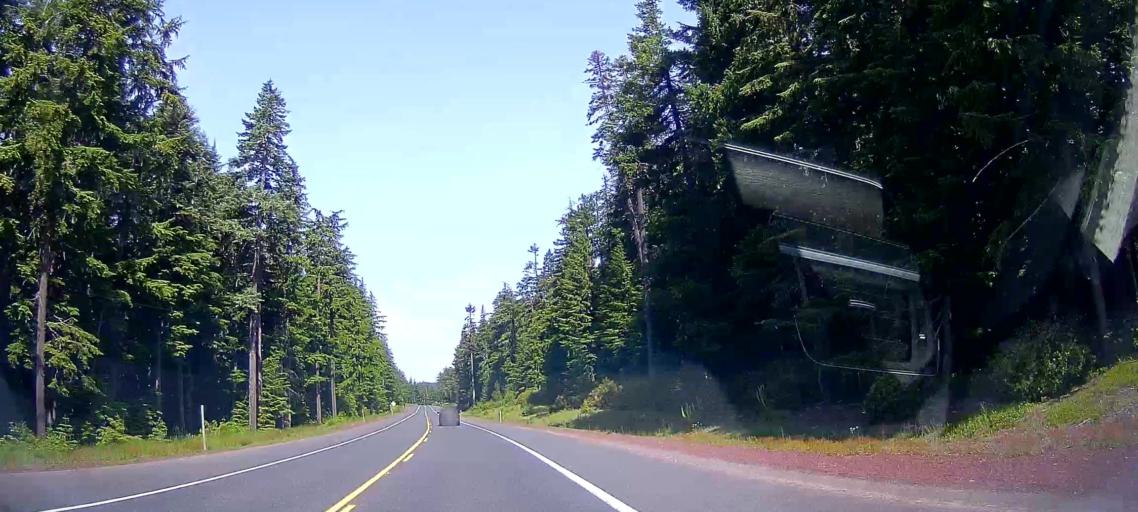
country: US
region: Oregon
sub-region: Clackamas County
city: Mount Hood Village
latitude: 45.1884
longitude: -121.6789
